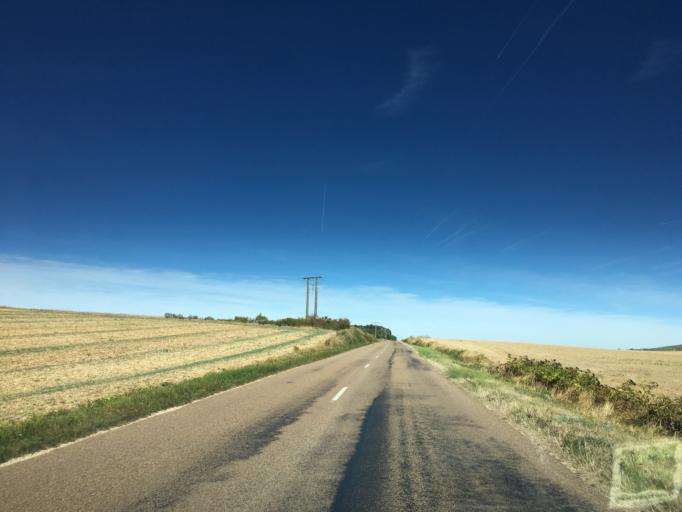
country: FR
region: Bourgogne
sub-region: Departement de l'Yonne
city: Vermenton
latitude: 47.6672
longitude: 3.6610
